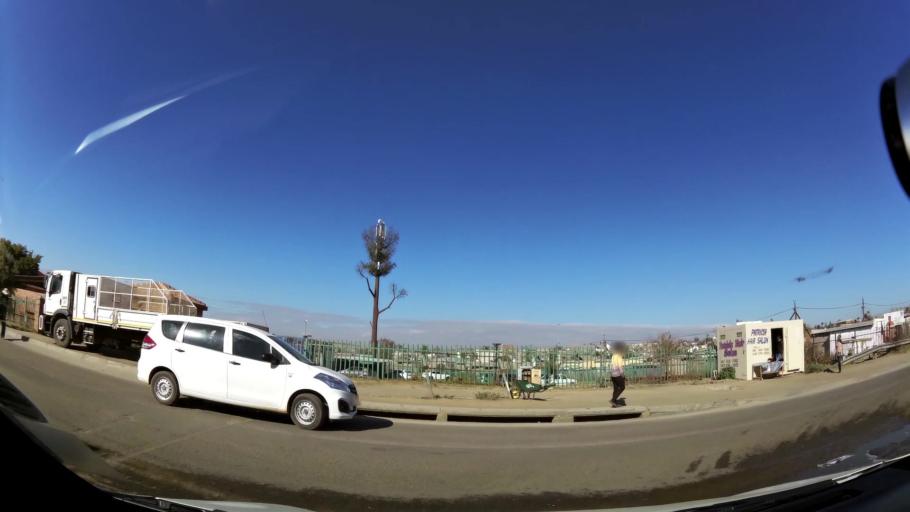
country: ZA
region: Gauteng
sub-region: City of Johannesburg Metropolitan Municipality
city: Diepsloot
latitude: -25.9109
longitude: 28.0928
